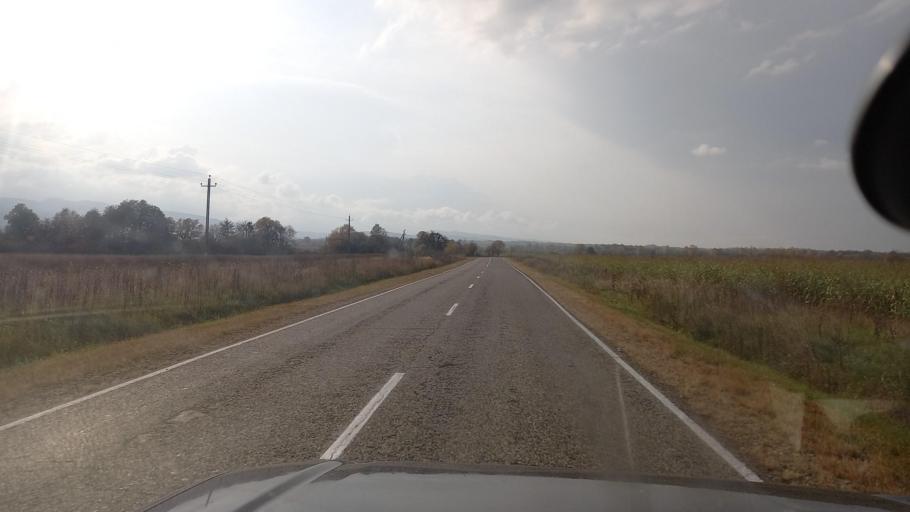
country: RU
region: Krasnodarskiy
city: Gubskaya
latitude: 44.3155
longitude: 40.5803
